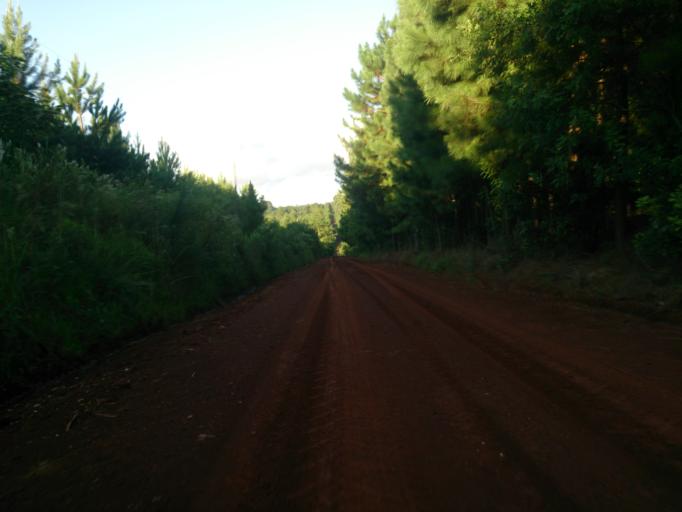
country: AR
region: Misiones
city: Florentino Ameghino
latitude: -27.5680
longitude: -55.1682
